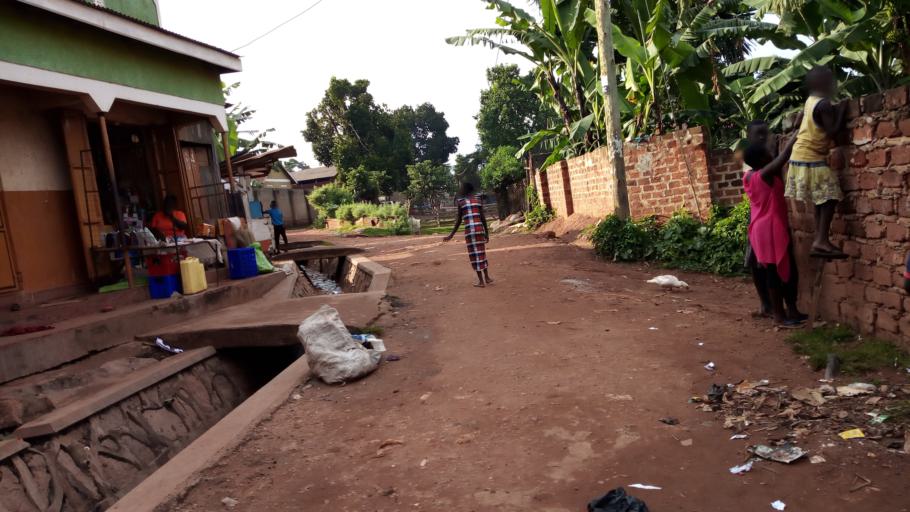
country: UG
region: Central Region
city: Kampala Central Division
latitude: 0.3734
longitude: 32.5530
